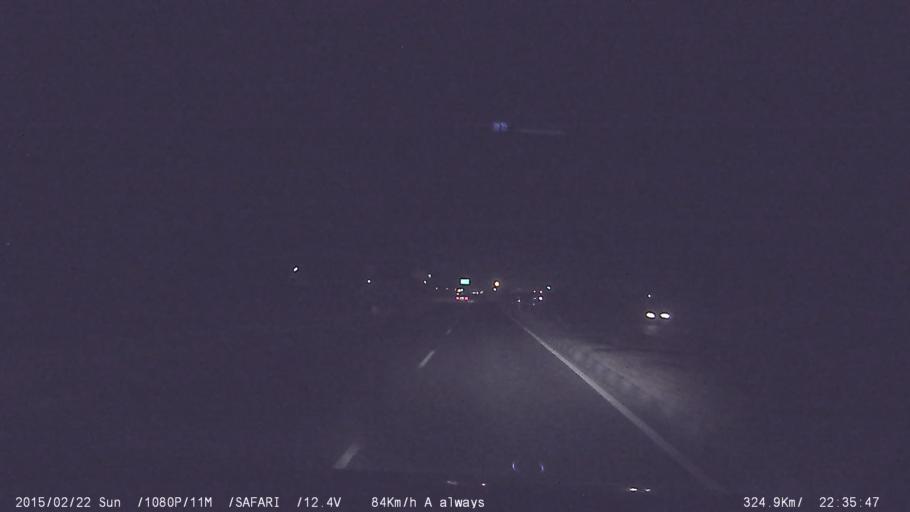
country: IN
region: Tamil Nadu
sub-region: Namakkal
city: Velur
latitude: 11.1380
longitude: 78.0194
